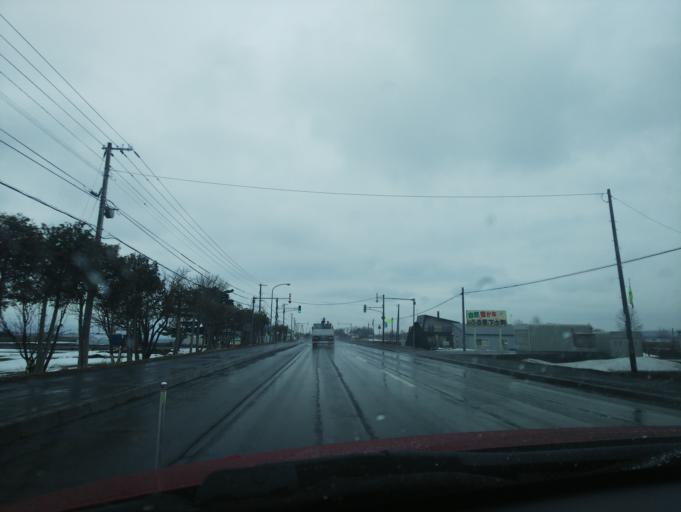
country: JP
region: Hokkaido
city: Nayoro
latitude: 44.2117
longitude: 142.3949
